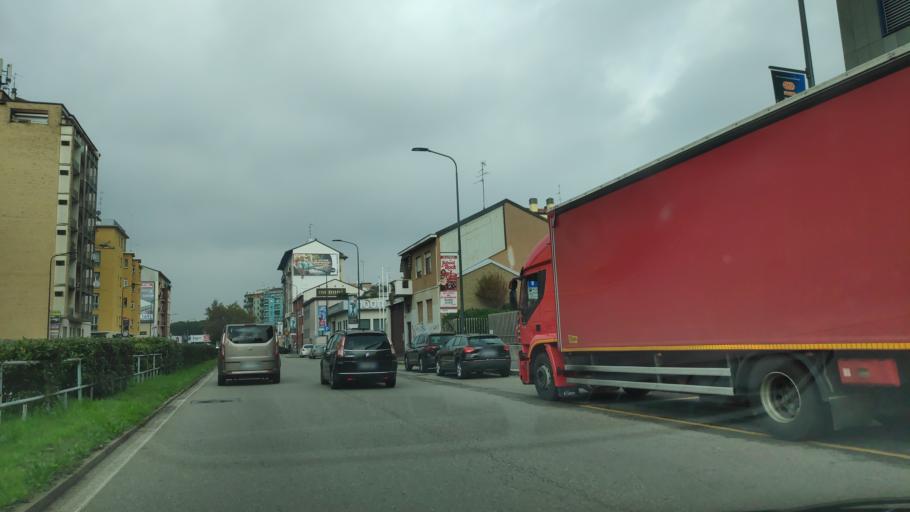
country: IT
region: Lombardy
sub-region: Citta metropolitana di Milano
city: Milano
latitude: 45.4410
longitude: 9.1726
